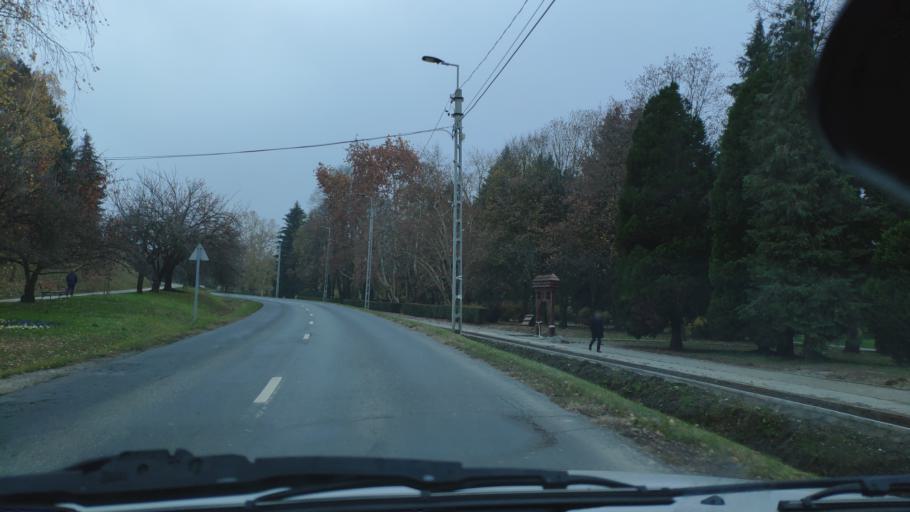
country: HU
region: Zala
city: Zalakomar
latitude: 46.5548
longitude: 17.1214
